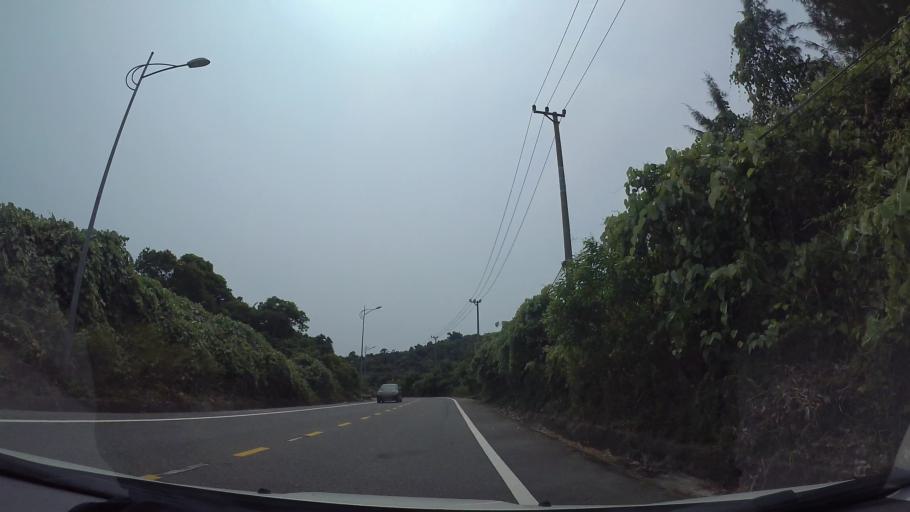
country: VN
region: Da Nang
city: Son Tra
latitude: 16.1002
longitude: 108.3075
